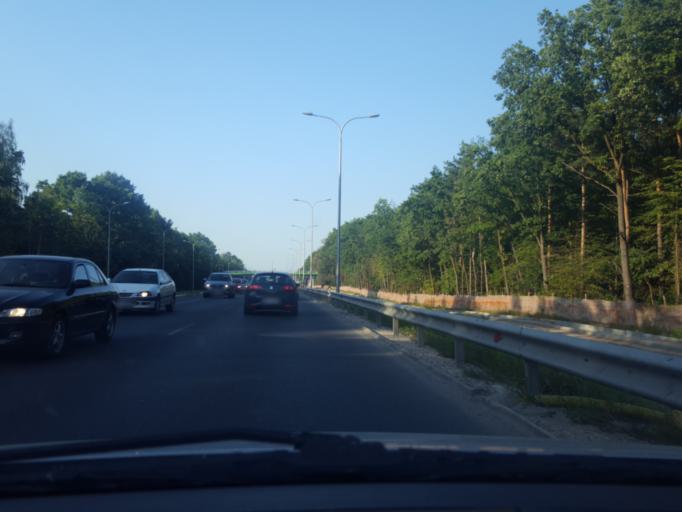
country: PL
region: Masovian Voivodeship
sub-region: Warszawa
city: Rembertow
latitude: 52.2495
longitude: 21.1386
